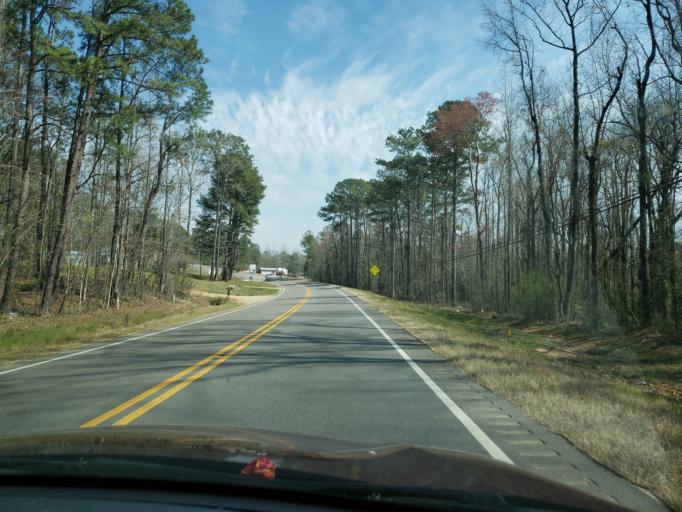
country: US
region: Alabama
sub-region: Elmore County
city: Wetumpka
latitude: 32.5650
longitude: -86.1290
